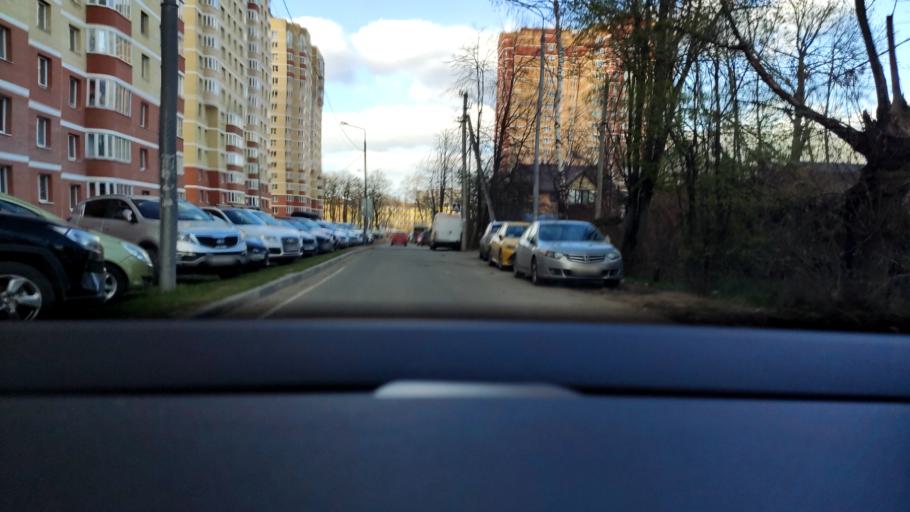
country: RU
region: Moskovskaya
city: Reutov
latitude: 55.7741
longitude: 37.8922
